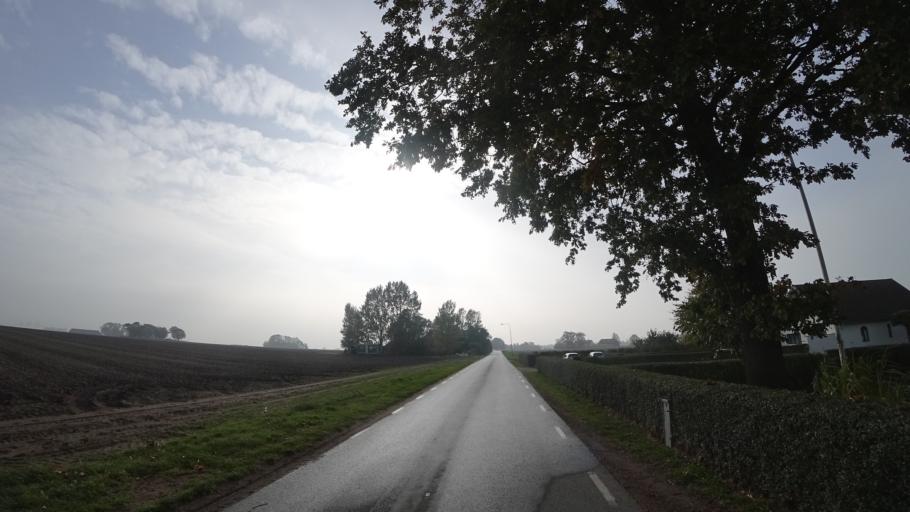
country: SE
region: Skane
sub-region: Kavlinge Kommun
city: Hofterup
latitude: 55.7885
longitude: 12.9807
